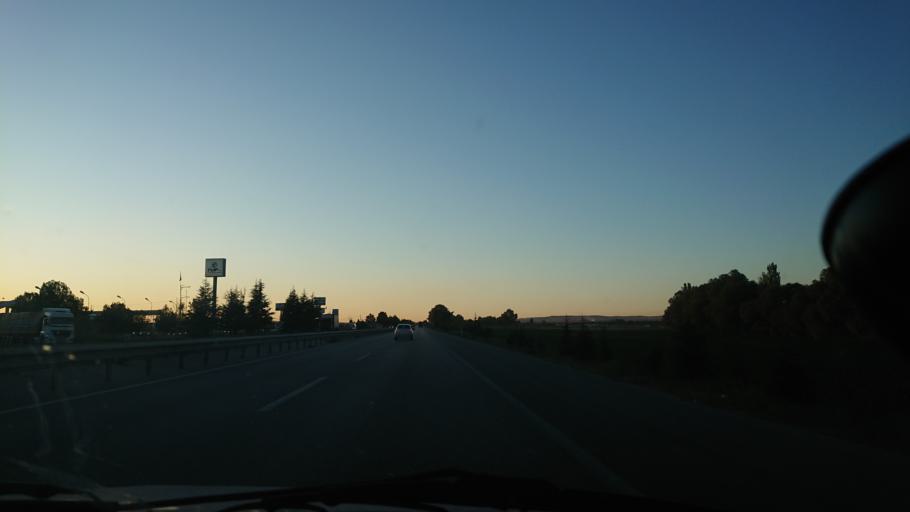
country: TR
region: Eskisehir
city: Alpu
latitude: 39.6271
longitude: 30.8240
